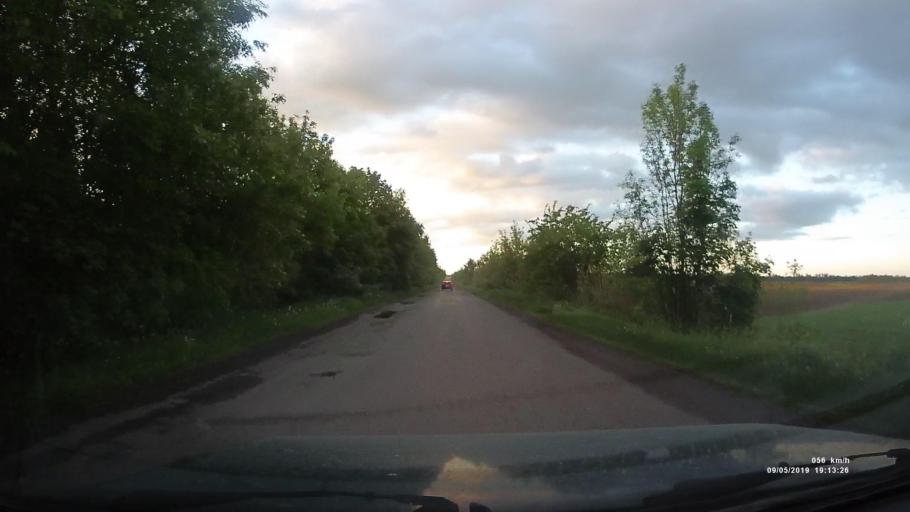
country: RU
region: Krasnodarskiy
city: Kanelovskaya
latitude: 46.7506
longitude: 39.2138
